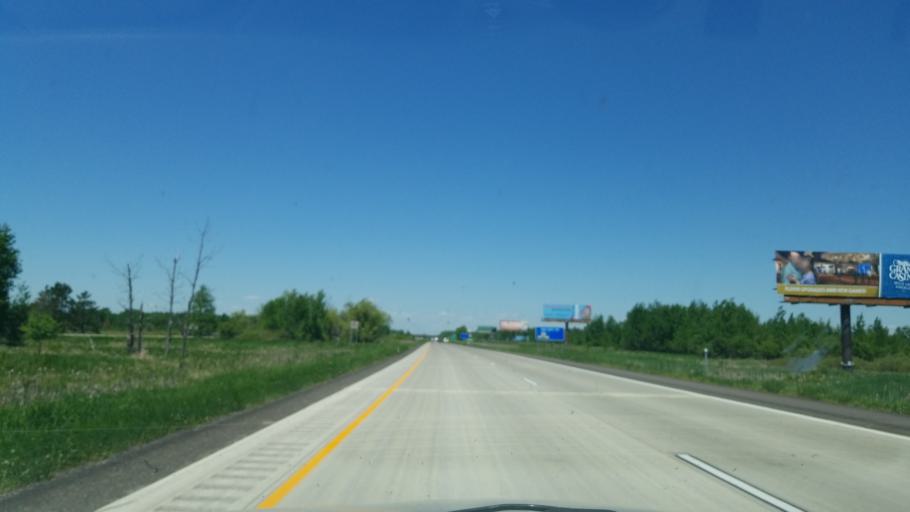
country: US
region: Minnesota
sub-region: Pine County
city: Pine City
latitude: 45.8936
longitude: -92.9667
